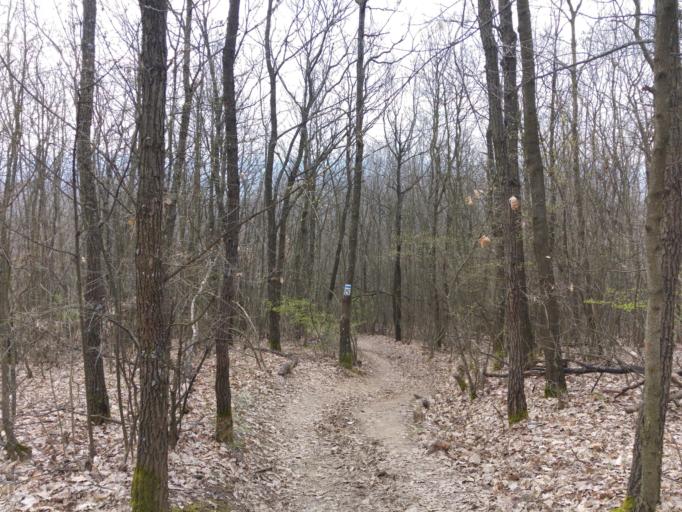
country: HU
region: Pest
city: Kosd
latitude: 47.8292
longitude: 19.1728
